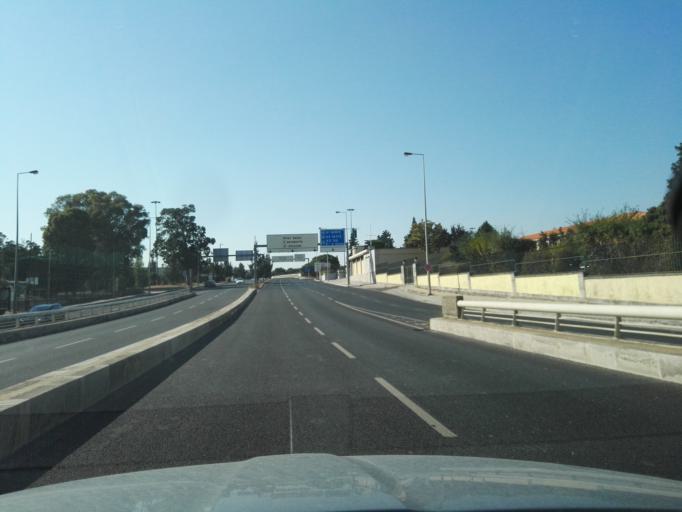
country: PT
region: Lisbon
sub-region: Loures
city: Sacavem
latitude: 38.7815
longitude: -9.1201
